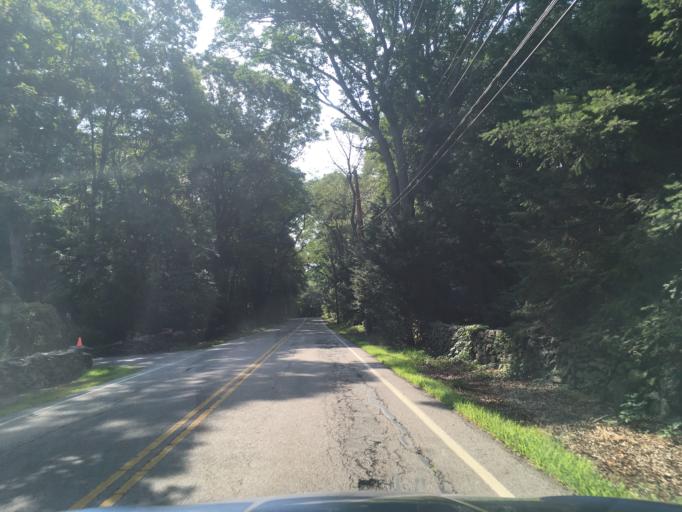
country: US
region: Rhode Island
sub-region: Kent County
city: East Greenwich
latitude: 41.6394
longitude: -71.4361
